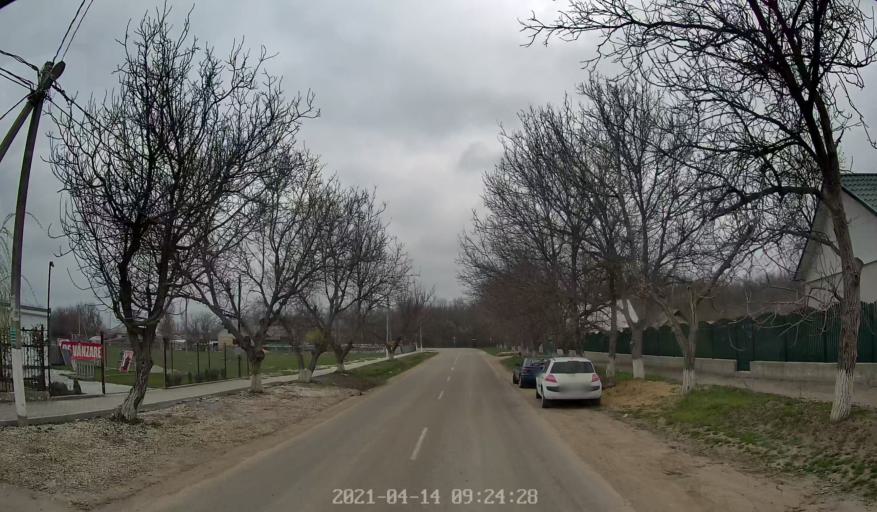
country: MD
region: Chisinau
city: Vadul lui Voda
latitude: 47.1095
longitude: 29.1144
